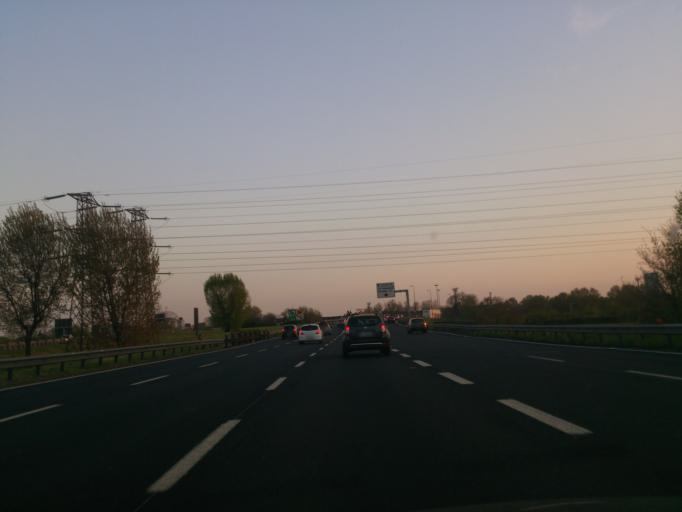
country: IT
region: Lombardy
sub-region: Citta metropolitana di Milano
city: Cologno Monzese
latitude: 45.5165
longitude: 9.2615
